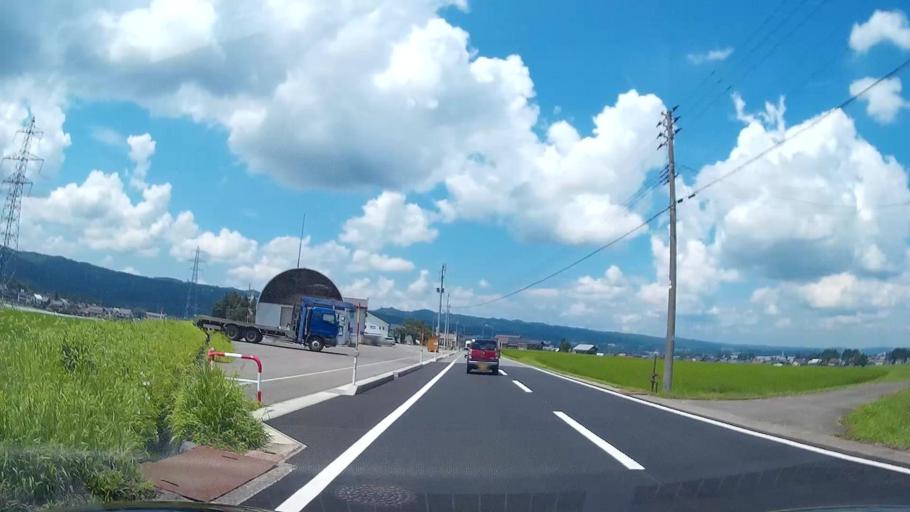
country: JP
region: Niigata
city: Tokamachi
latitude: 37.0978
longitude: 138.7392
